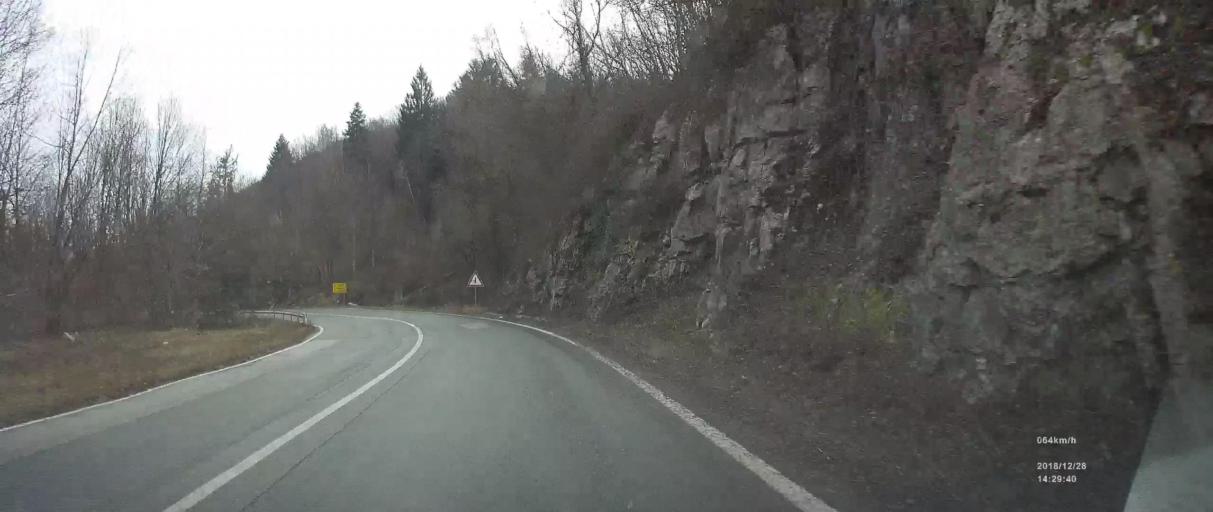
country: HR
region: Primorsko-Goranska
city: Vrbovsko
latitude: 45.4205
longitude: 15.1182
